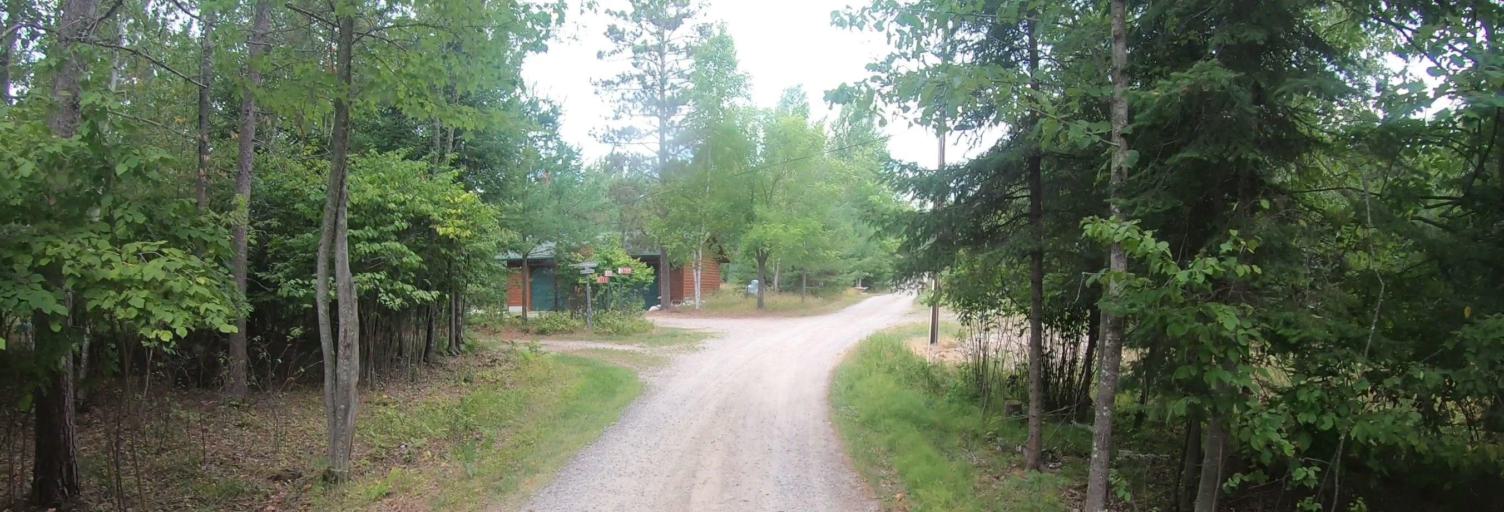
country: US
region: Minnesota
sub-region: Saint Louis County
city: Mountain Iron
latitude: 47.9434
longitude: -92.6301
